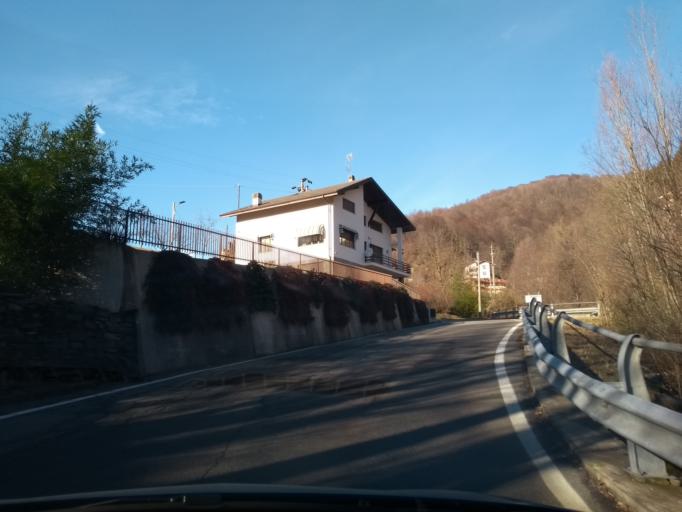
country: IT
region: Piedmont
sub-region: Provincia di Torino
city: Pessinetto
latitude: 45.2857
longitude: 7.4170
